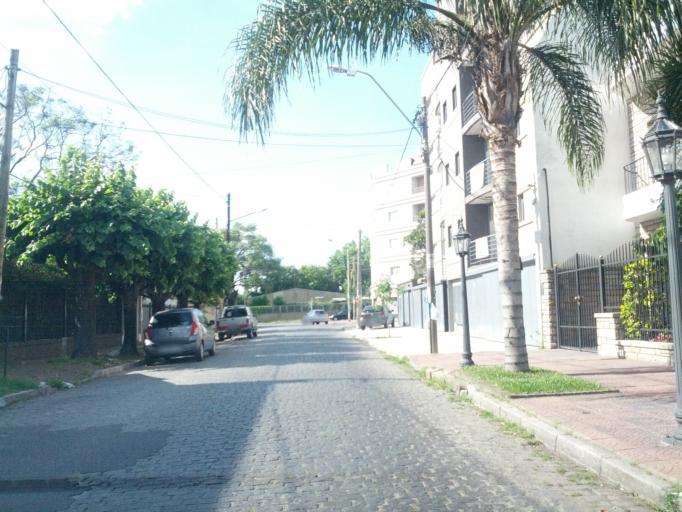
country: AR
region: Buenos Aires
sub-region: Partido de Moron
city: Moron
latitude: -34.6447
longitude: -58.5849
